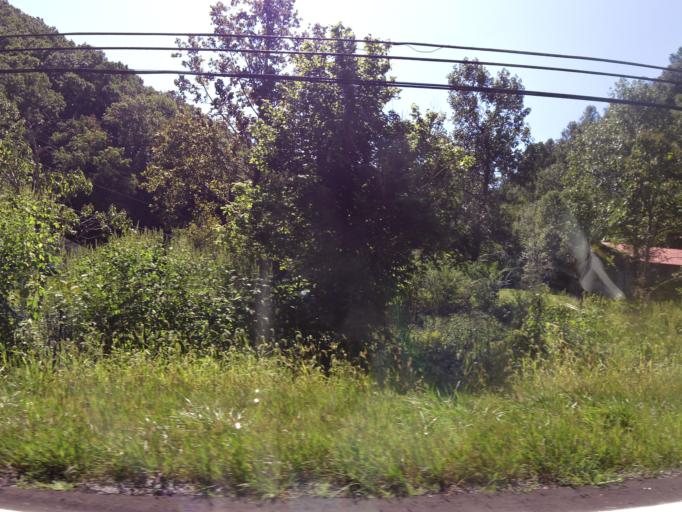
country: US
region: Kentucky
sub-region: Clay County
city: Manchester
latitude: 37.1170
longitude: -83.6412
